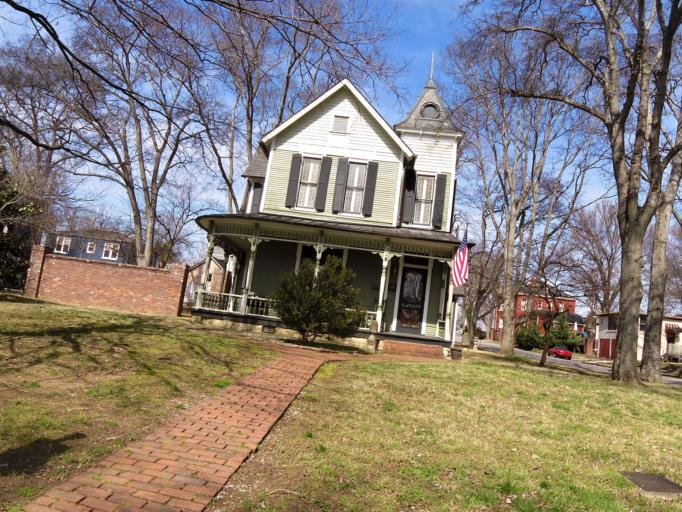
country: US
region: Tennessee
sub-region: Davidson County
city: Belle Meade
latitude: 36.1499
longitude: -86.8435
